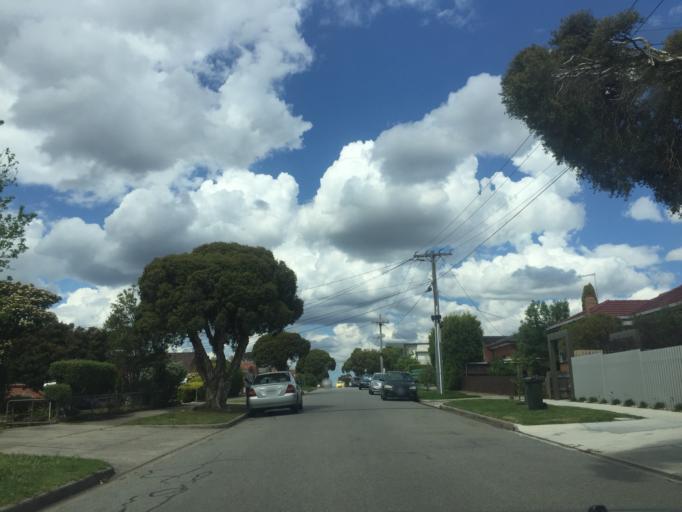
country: AU
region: Victoria
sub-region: Darebin
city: Kingsbury
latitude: -37.7232
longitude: 145.0251
